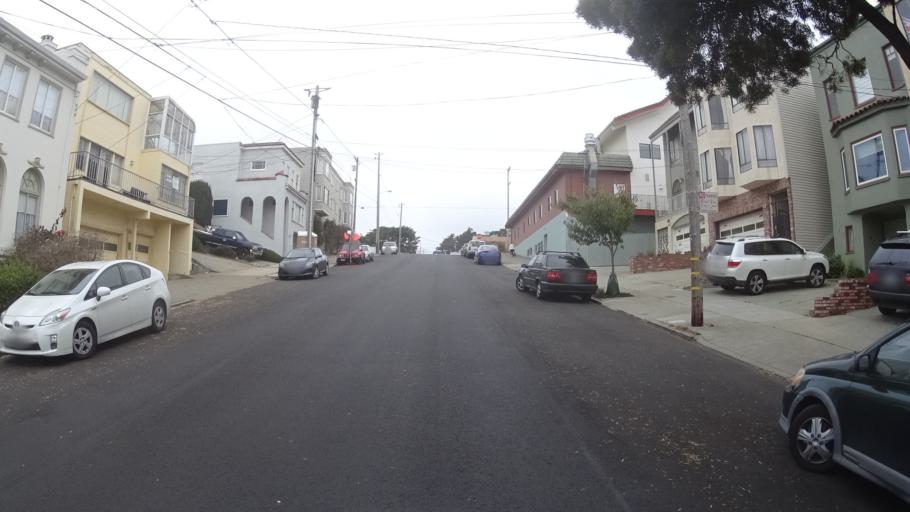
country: US
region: California
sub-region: Marin County
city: Sausalito
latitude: 37.7784
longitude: -122.5029
